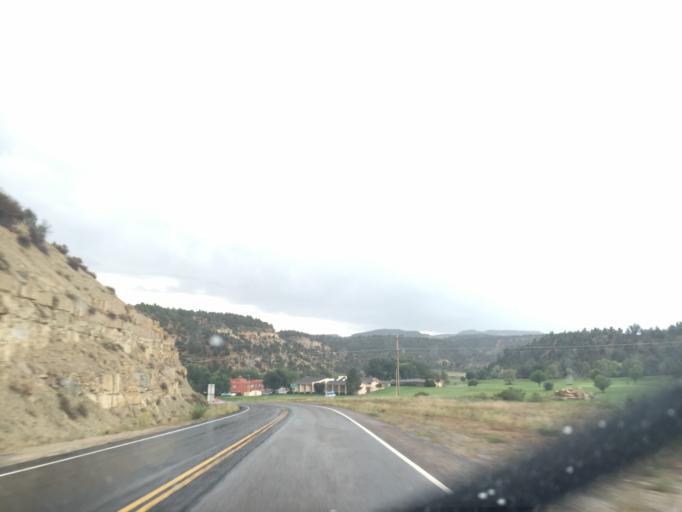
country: US
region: Utah
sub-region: Kane County
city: Kanab
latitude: 37.2259
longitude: -112.6840
